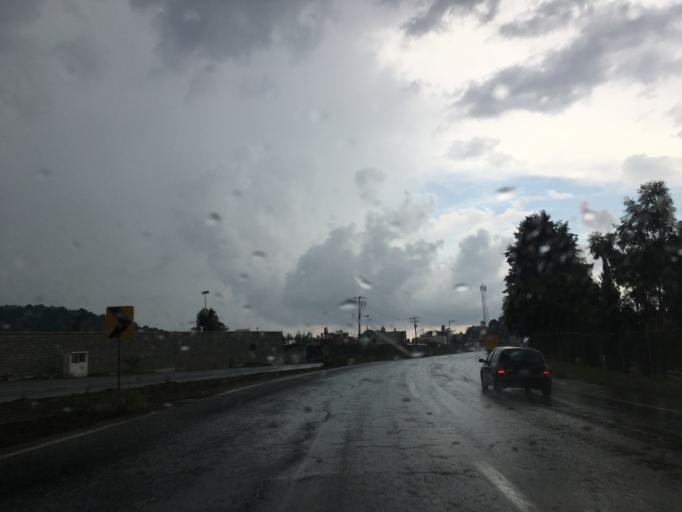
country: MX
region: Michoacan
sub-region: Uruapan
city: Uruapan
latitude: 19.4402
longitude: -102.0713
